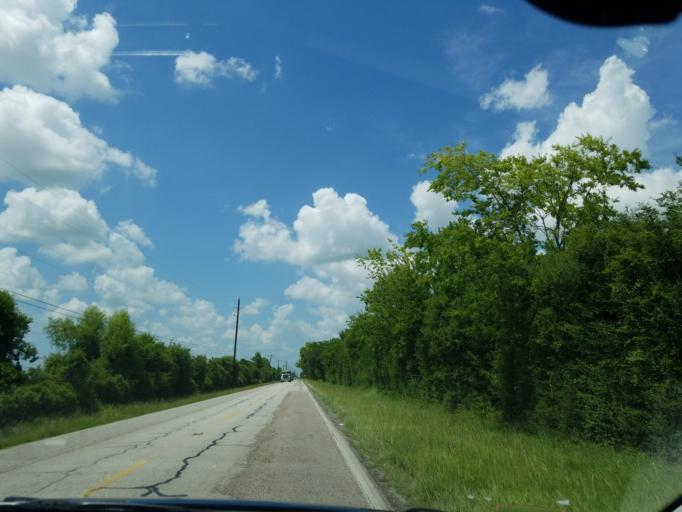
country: US
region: Texas
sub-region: Harris County
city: Katy
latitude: 29.8702
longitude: -95.8072
